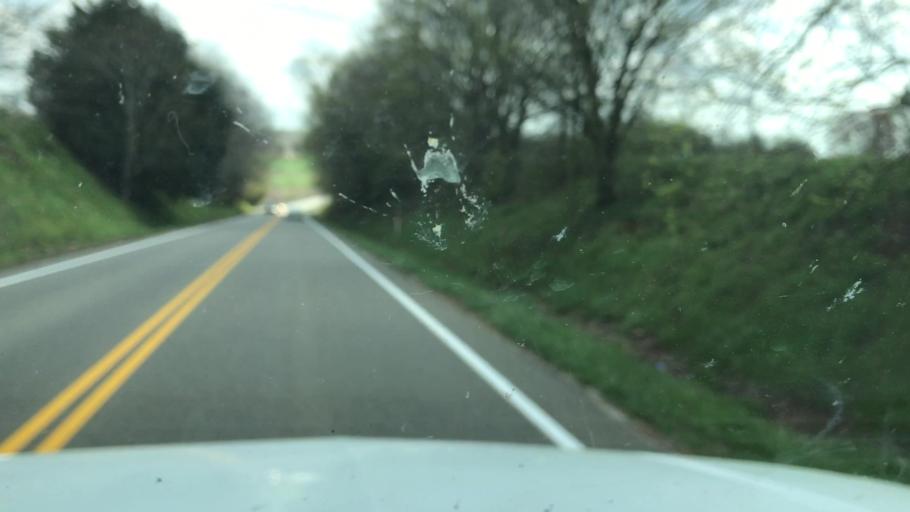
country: US
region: Virginia
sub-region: Goochland County
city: Goochland
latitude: 37.6483
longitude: -77.8340
